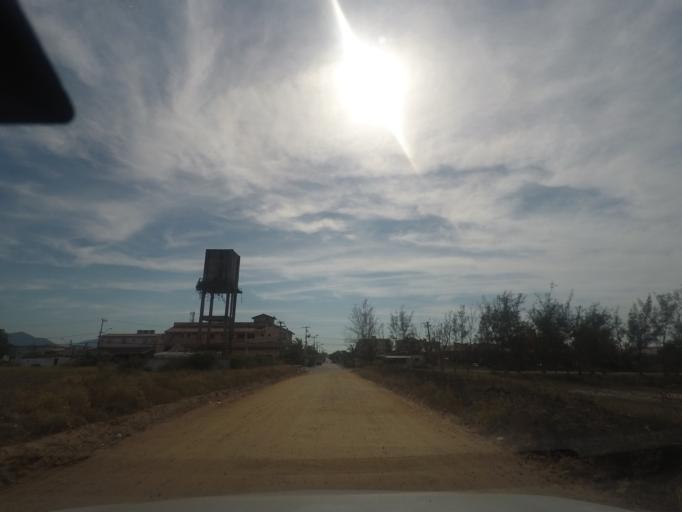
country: BR
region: Rio de Janeiro
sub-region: Marica
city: Marica
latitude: -22.9594
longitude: -42.8283
